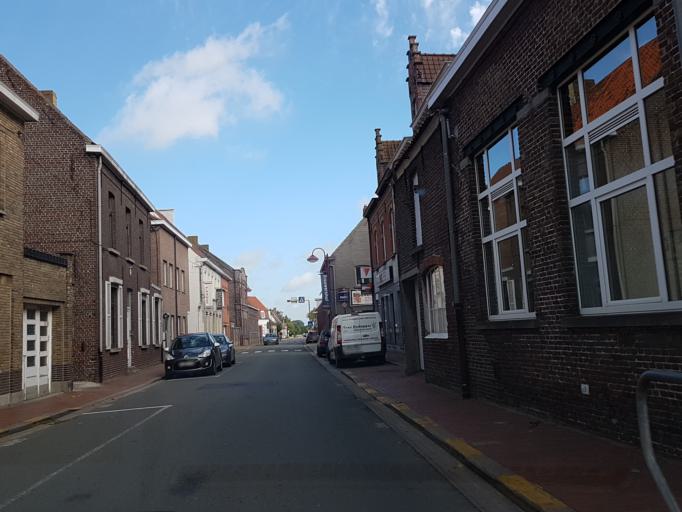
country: BE
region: Flanders
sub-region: Provincie Oost-Vlaanderen
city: Nevele
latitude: 51.0752
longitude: 3.5356
